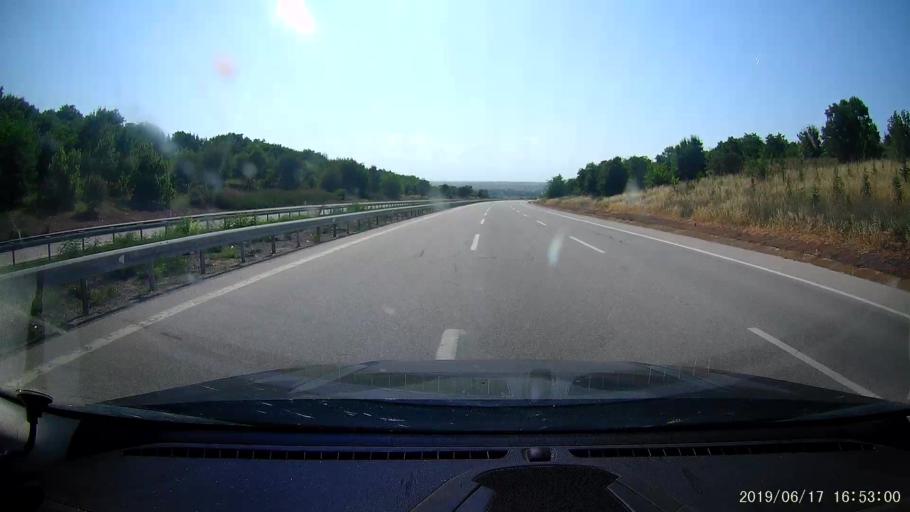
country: TR
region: Kirklareli
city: Inece
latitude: 41.5600
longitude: 27.0361
